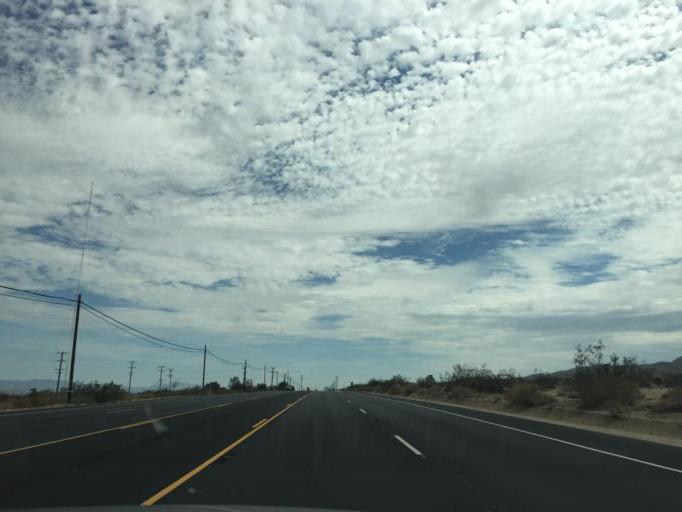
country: US
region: California
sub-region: San Bernardino County
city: Twentynine Palms
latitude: 34.1351
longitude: -116.1738
